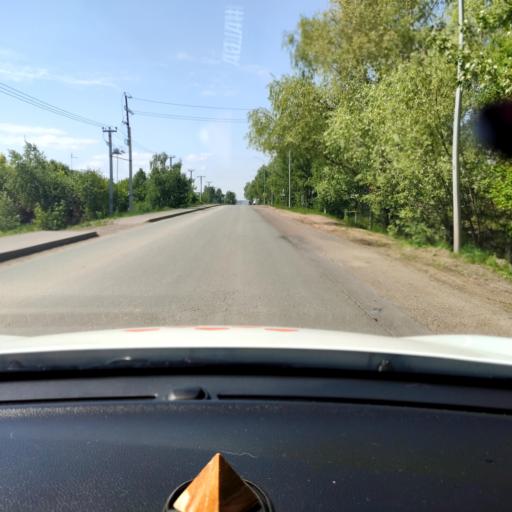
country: RU
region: Tatarstan
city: Stolbishchi
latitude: 55.6986
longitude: 49.1861
